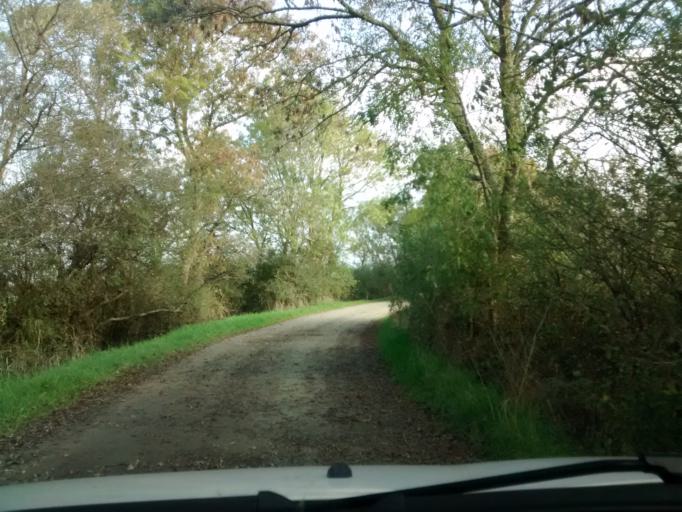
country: FR
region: Pays de la Loire
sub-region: Departement de la Loire-Atlantique
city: Cordemais
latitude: 47.2519
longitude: -1.8627
